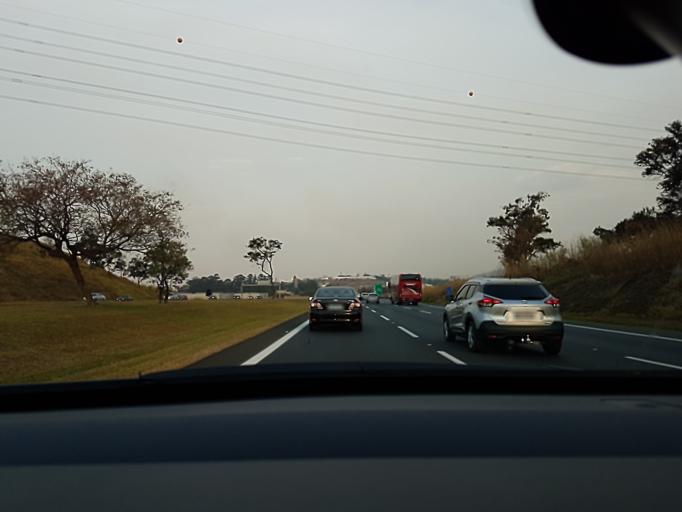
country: BR
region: Sao Paulo
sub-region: Jundiai
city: Jundiai
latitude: -23.1614
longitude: -46.9493
